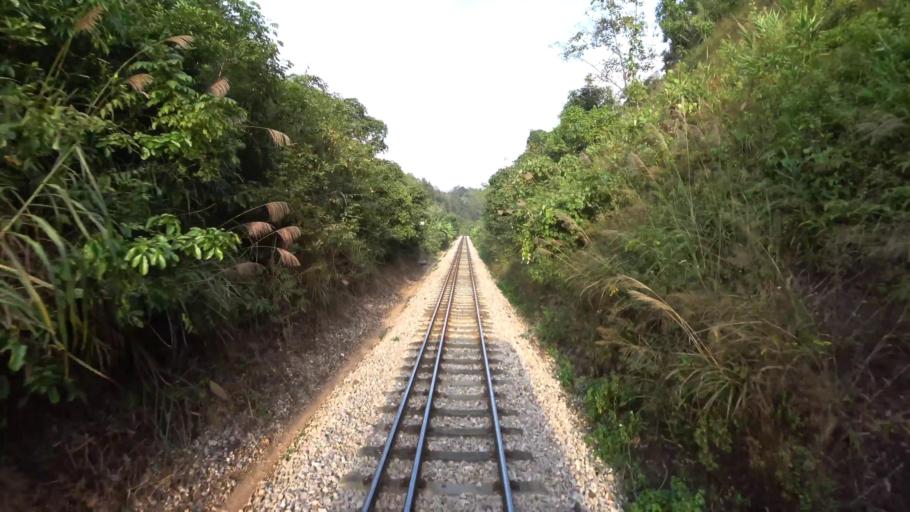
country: VN
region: Lang Son
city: Thi Tran Cao Loc
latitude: 21.9245
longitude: 106.7121
